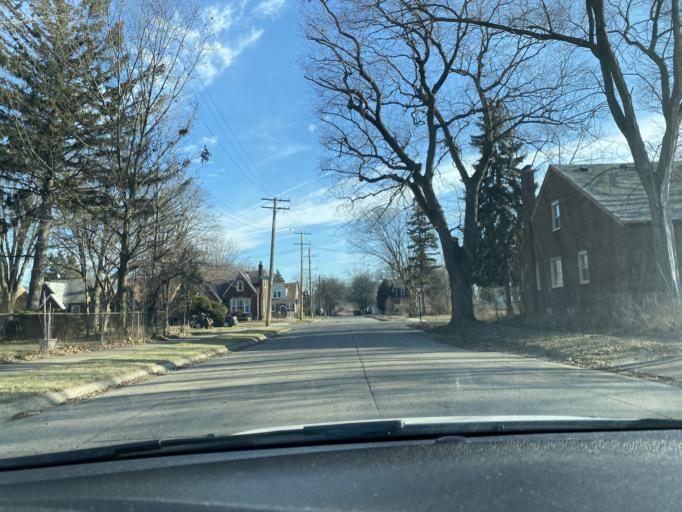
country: US
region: Michigan
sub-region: Wayne County
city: Harper Woods
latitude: 42.4115
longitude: -82.9518
